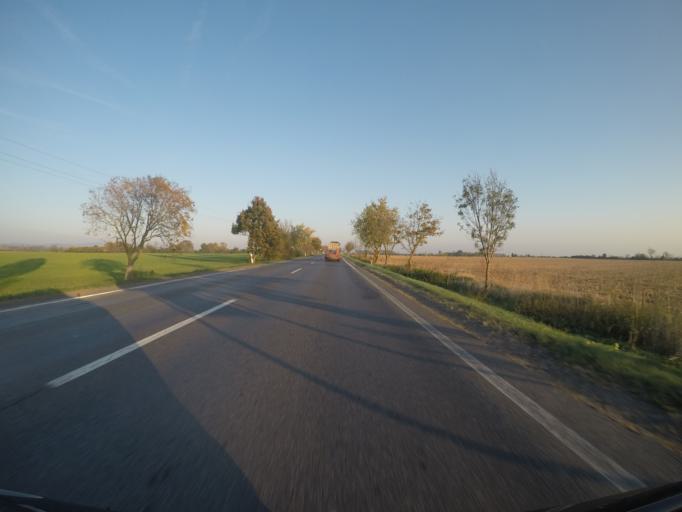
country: HU
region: Baranya
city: Szentlorinc
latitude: 46.0419
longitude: 17.9218
